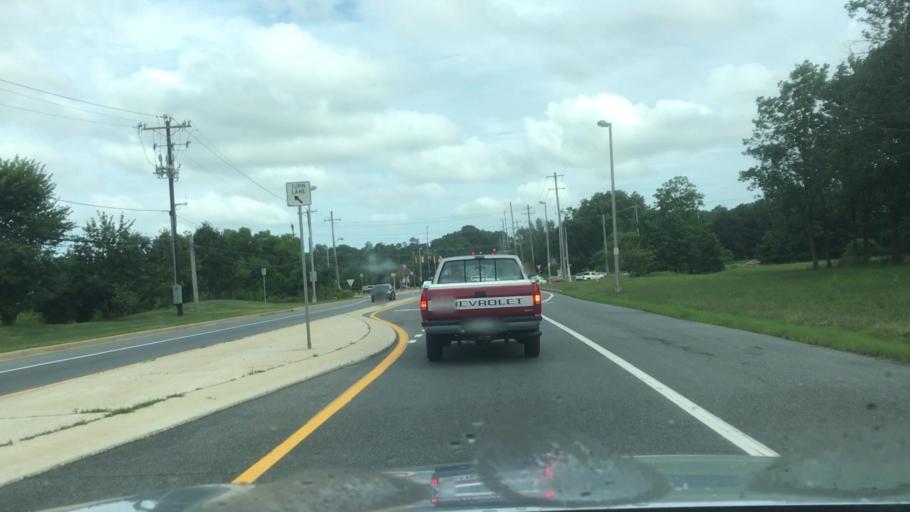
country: US
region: Delaware
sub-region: New Castle County
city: North Star
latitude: 39.7755
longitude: -75.7166
